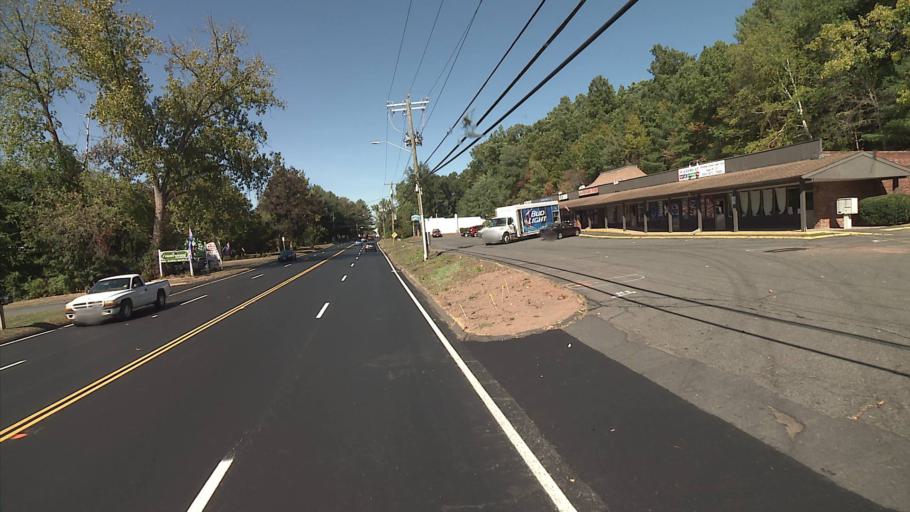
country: US
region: Connecticut
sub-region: Tolland County
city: Rockville
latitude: 41.8562
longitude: -72.4843
